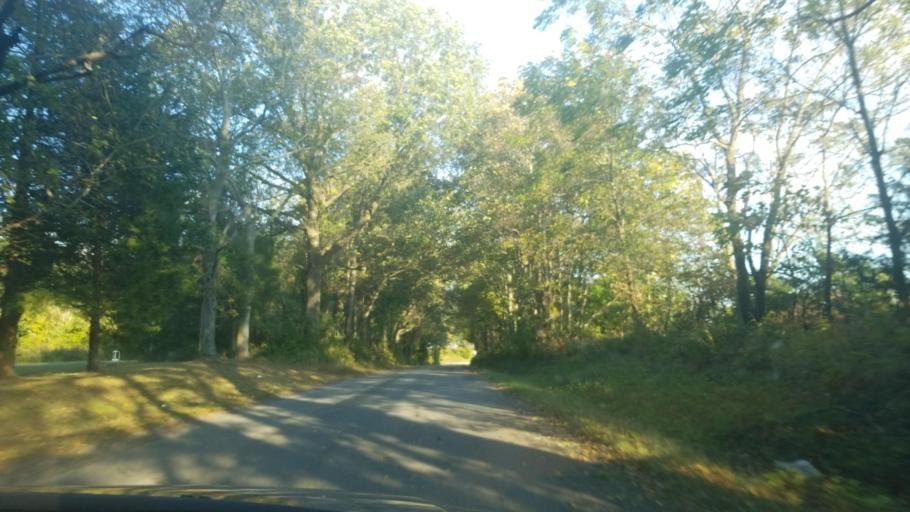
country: US
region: Illinois
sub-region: Williamson County
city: Marion
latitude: 37.7610
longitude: -88.8017
